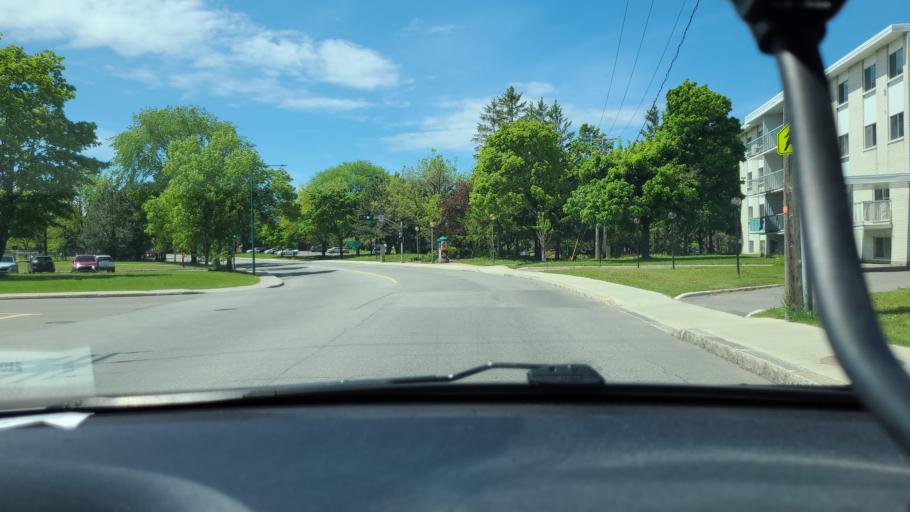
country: CA
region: Quebec
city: L'Ancienne-Lorette
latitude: 46.7678
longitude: -71.3246
